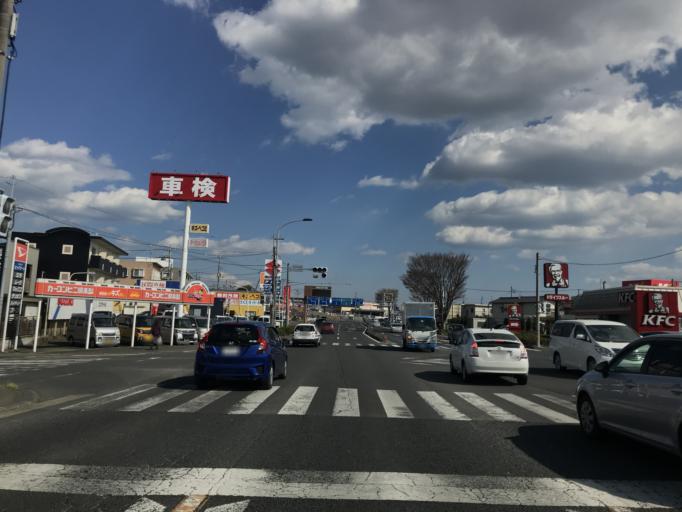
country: JP
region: Ibaraki
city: Mito-shi
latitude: 36.3420
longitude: 140.4794
